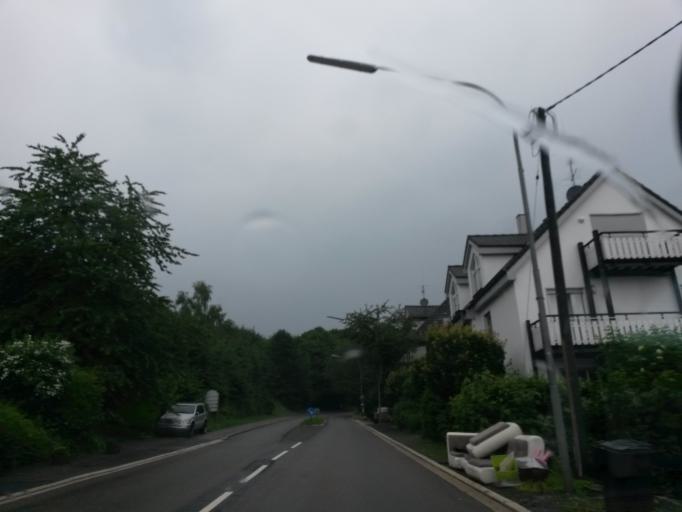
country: DE
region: North Rhine-Westphalia
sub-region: Regierungsbezirk Koln
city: Gummersbach
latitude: 51.0482
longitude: 7.5460
